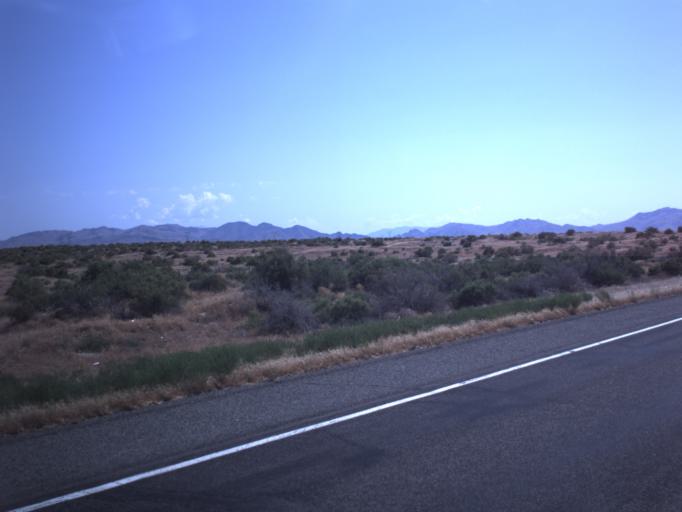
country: US
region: Utah
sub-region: Millard County
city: Delta
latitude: 39.4783
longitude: -112.4994
